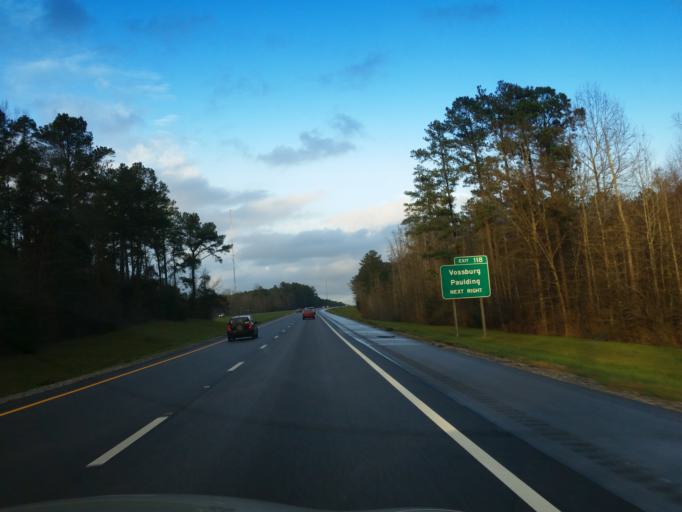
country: US
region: Mississippi
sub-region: Jones County
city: Sharon
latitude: 31.9567
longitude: -88.9752
